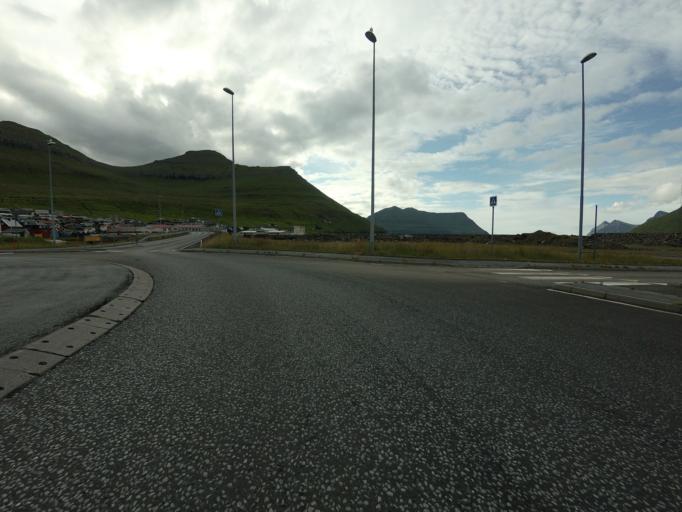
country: FO
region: Eysturoy
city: Eystur
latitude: 62.2112
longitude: -6.7009
